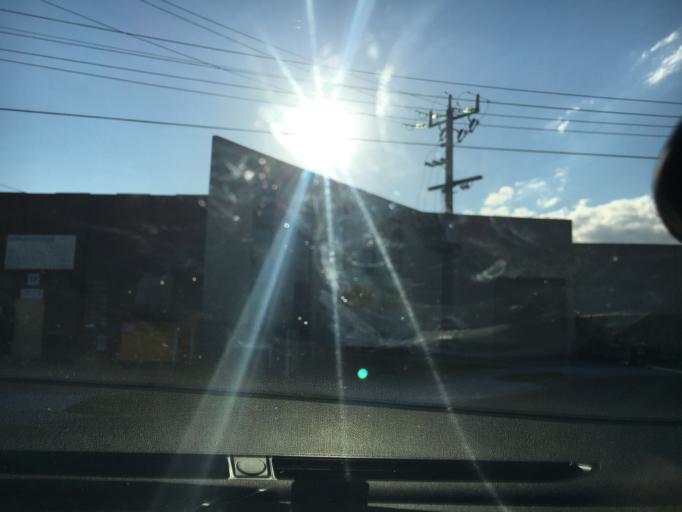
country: AU
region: Victoria
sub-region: Kingston
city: Clayton South
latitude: -37.9324
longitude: 145.1208
